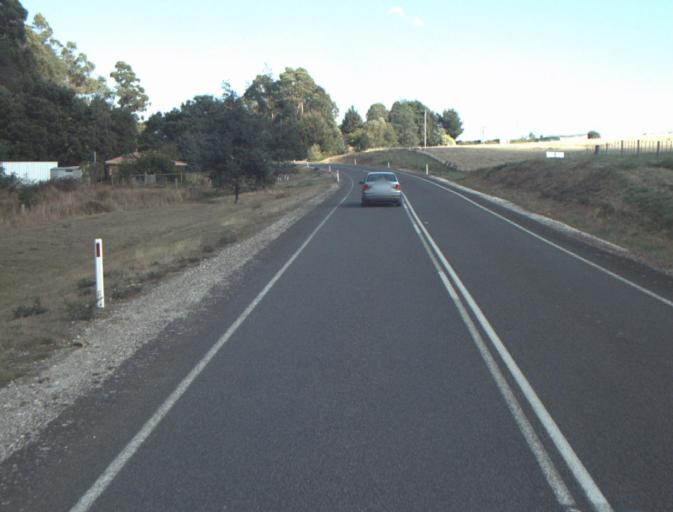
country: AU
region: Tasmania
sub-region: Launceston
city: Mayfield
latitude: -41.2812
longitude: 147.2195
